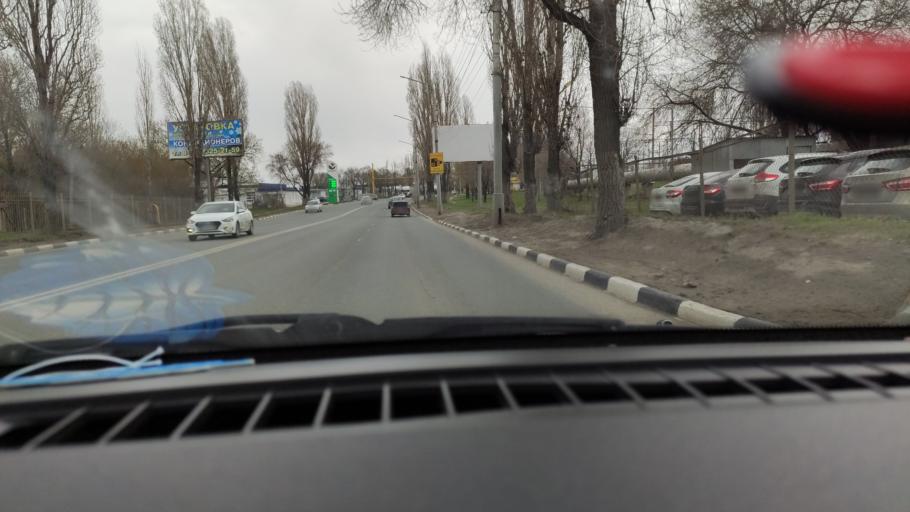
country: RU
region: Saratov
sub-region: Saratovskiy Rayon
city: Saratov
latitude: 51.5783
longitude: 45.9852
